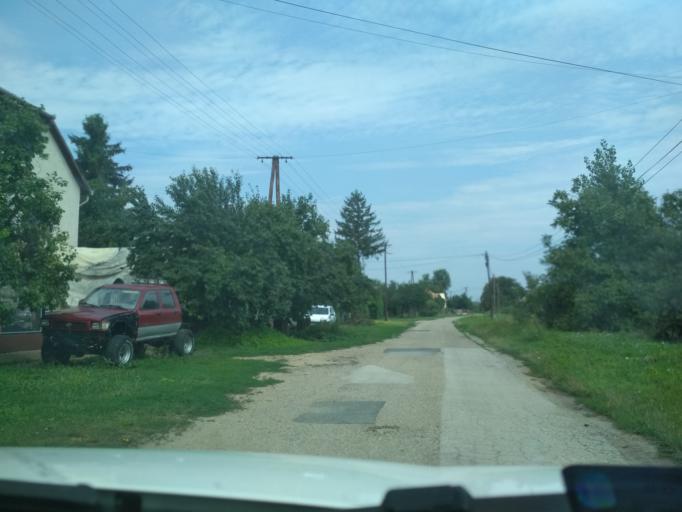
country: HU
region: Jasz-Nagykun-Szolnok
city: Tiszafured
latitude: 47.6229
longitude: 20.7585
